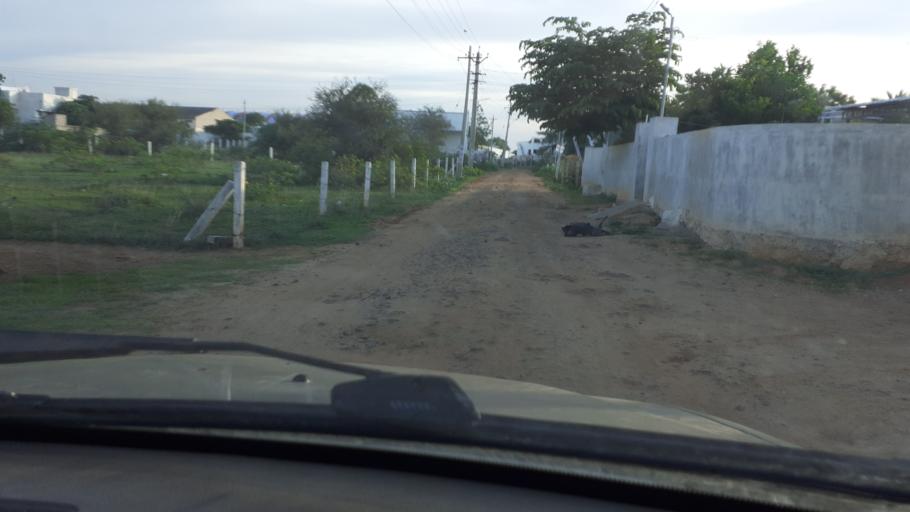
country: IN
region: Tamil Nadu
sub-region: Tirunelveli Kattabo
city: Tirunelveli
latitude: 8.6716
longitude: 77.7168
